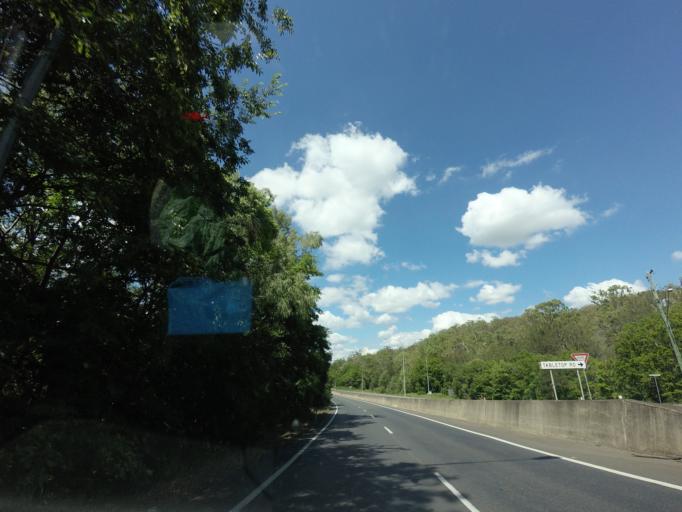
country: AU
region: Queensland
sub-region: Toowoomba
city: East Toowoomba
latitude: -27.5625
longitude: 152.0039
